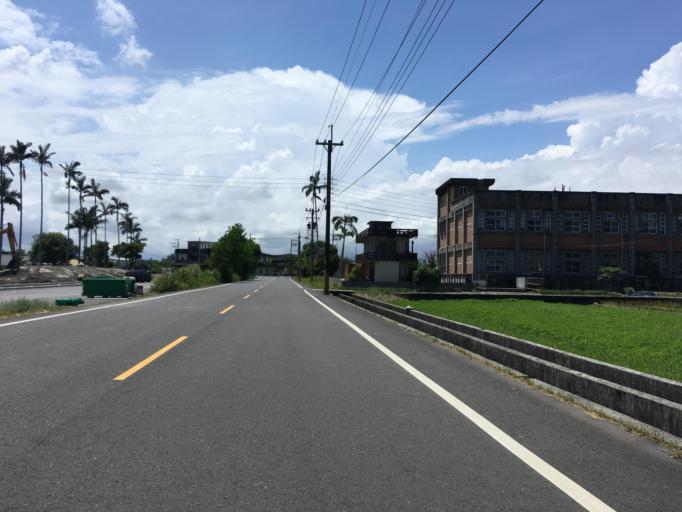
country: TW
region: Taiwan
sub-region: Yilan
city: Yilan
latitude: 24.6879
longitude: 121.8050
